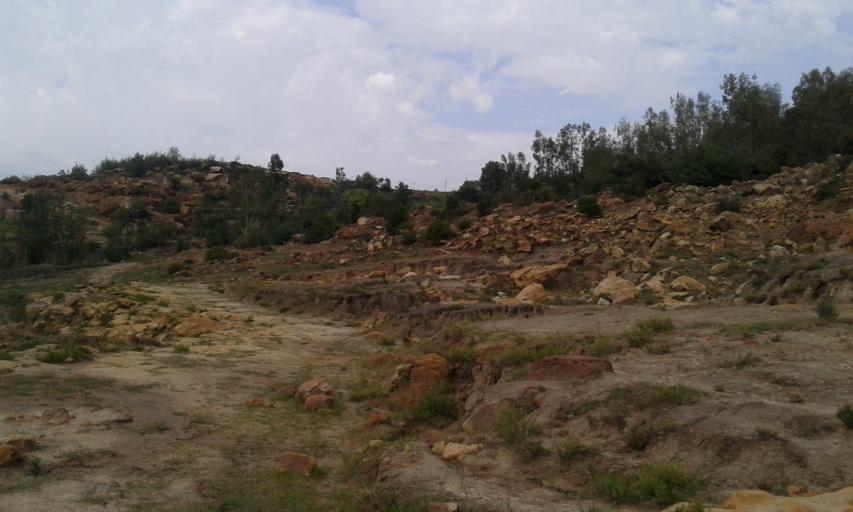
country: LS
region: Maseru
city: Maseru
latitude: -29.4230
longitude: 27.5761
